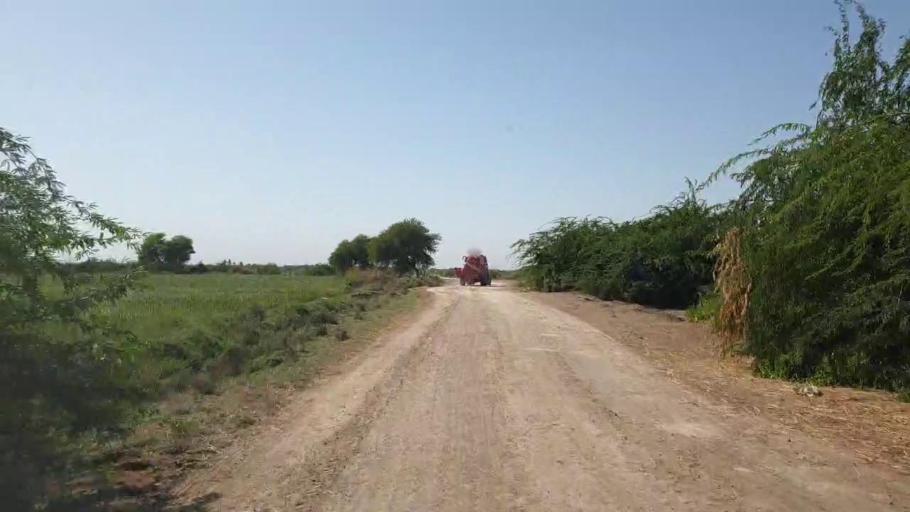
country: PK
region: Sindh
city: Tando Bago
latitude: 24.7054
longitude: 69.0183
